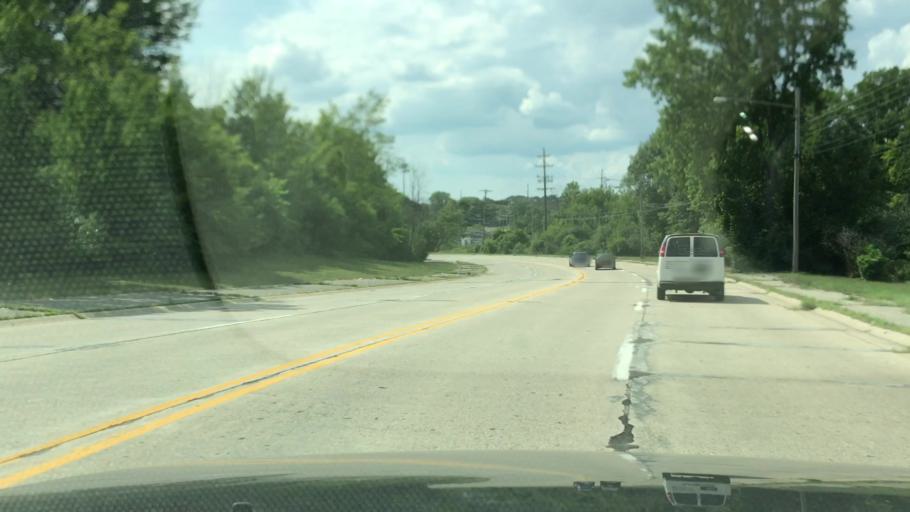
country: US
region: Michigan
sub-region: Kent County
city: East Grand Rapids
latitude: 42.9693
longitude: -85.5917
